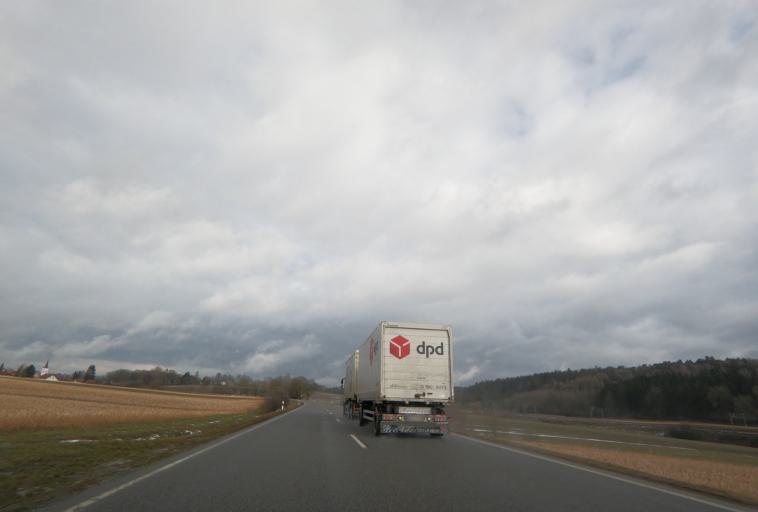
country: DE
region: Bavaria
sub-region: Lower Bavaria
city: Mallersdorf-Pfaffenberg
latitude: 48.7778
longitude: 12.1860
